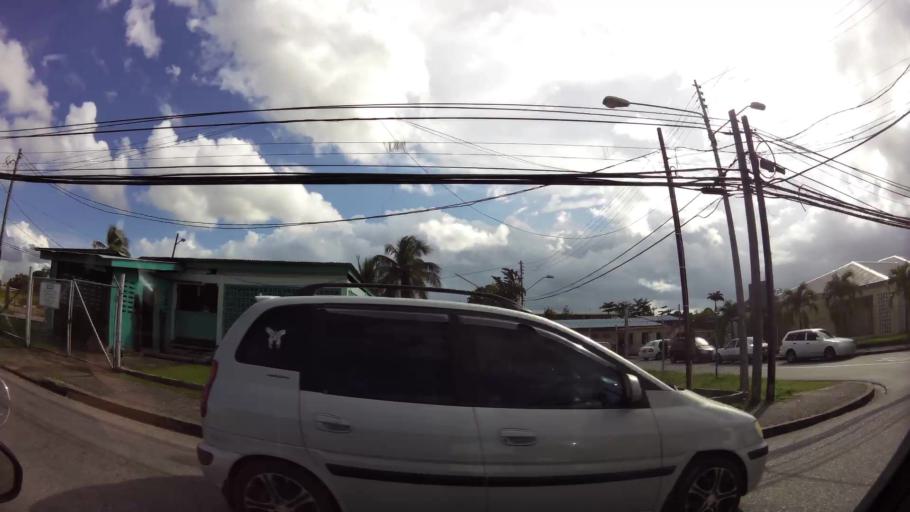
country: TT
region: City of San Fernando
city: Mon Repos
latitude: 10.2672
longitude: -61.4492
